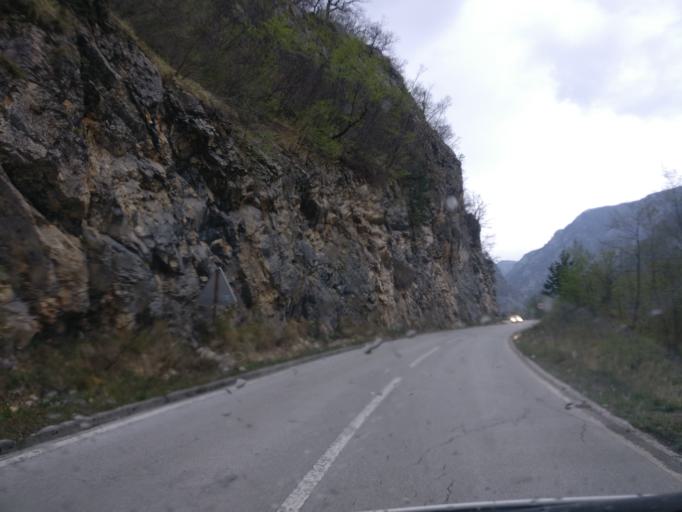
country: ME
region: Opstina Pluzine
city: Pluzine
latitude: 43.2097
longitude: 18.8592
